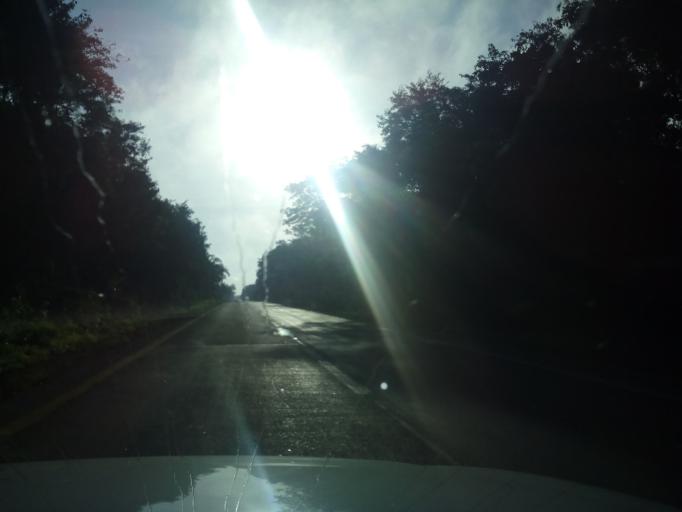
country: MX
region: Yucatan
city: Tunkas
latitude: 20.7643
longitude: -88.7956
